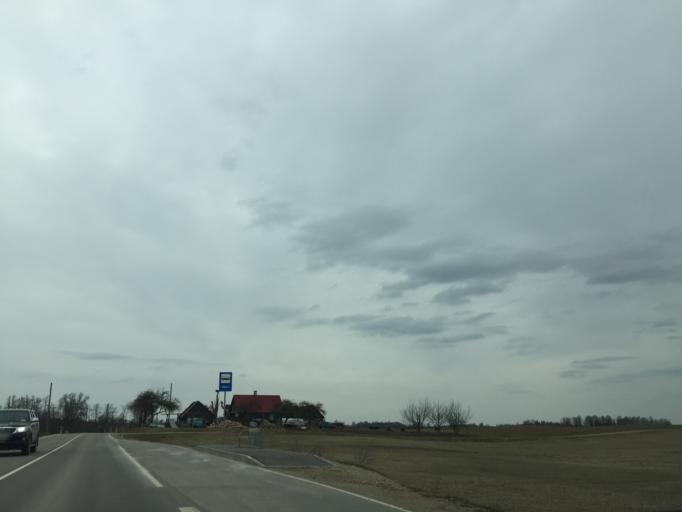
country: LV
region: Ilukste
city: Ilukste
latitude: 55.9973
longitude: 26.2857
